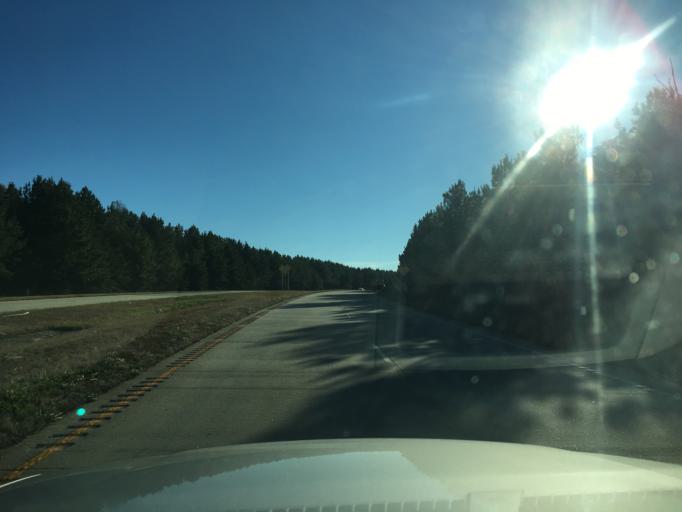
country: US
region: South Carolina
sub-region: Greenville County
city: Greer
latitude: 34.9172
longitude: -82.2053
